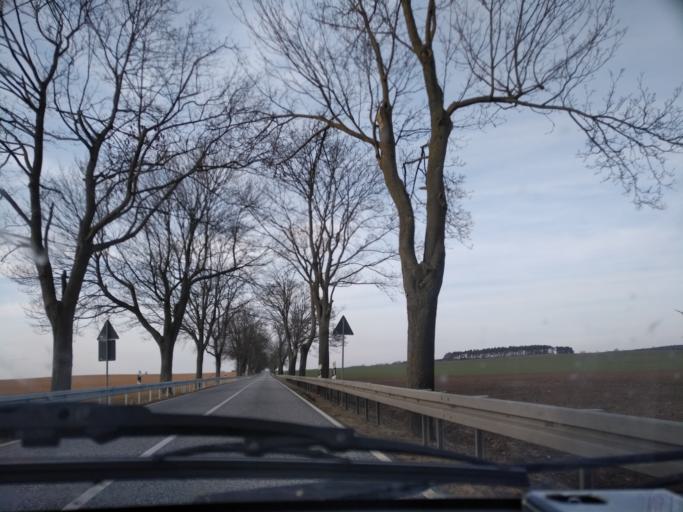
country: DE
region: Brandenburg
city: Juterbog
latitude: 51.9559
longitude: 13.1132
